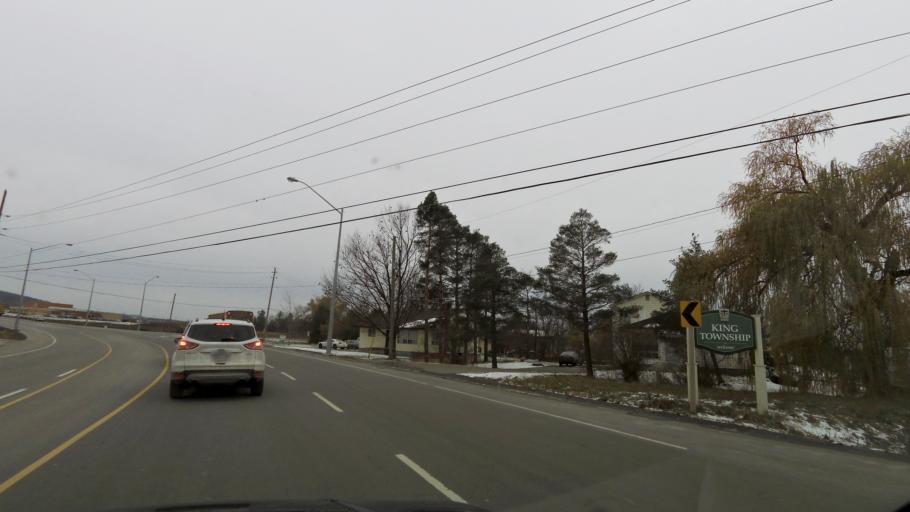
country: CA
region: Ontario
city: Newmarket
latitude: 44.1043
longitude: -79.5198
